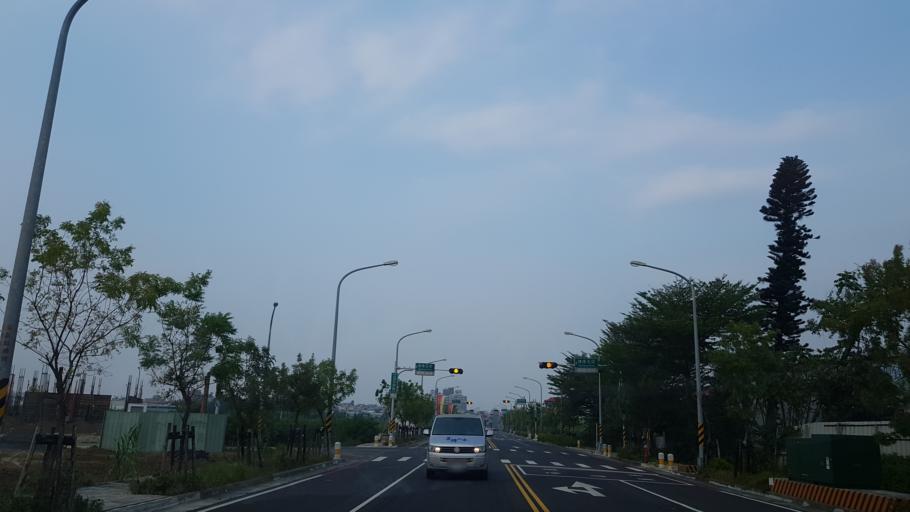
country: TW
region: Taiwan
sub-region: Chiayi
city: Jiayi Shi
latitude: 23.4480
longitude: 120.4405
